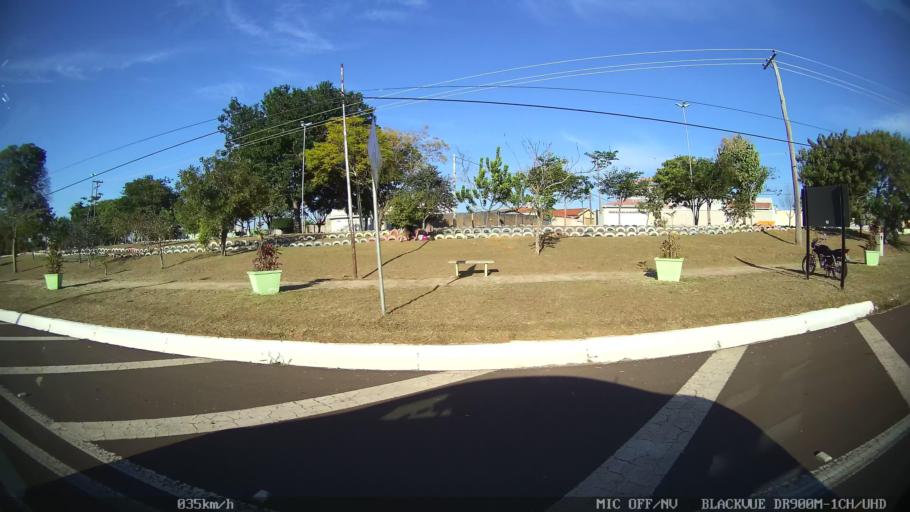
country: BR
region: Sao Paulo
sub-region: Franca
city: Franca
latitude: -20.5086
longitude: -47.3726
